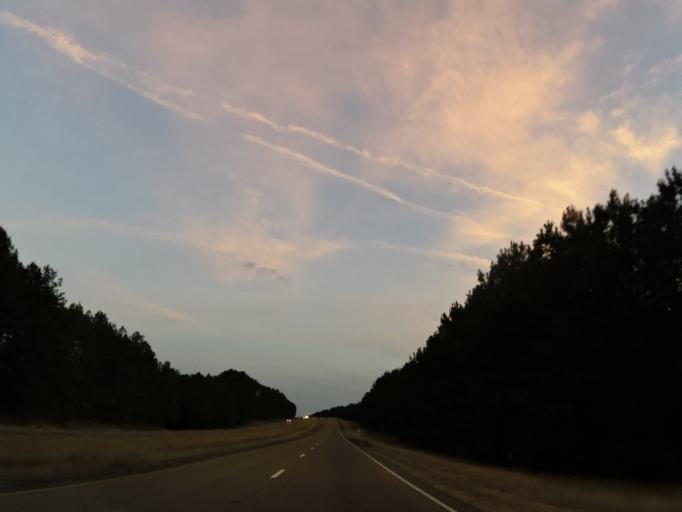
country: US
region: Mississippi
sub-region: Lauderdale County
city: Meridian Station
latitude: 32.6196
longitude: -88.4988
